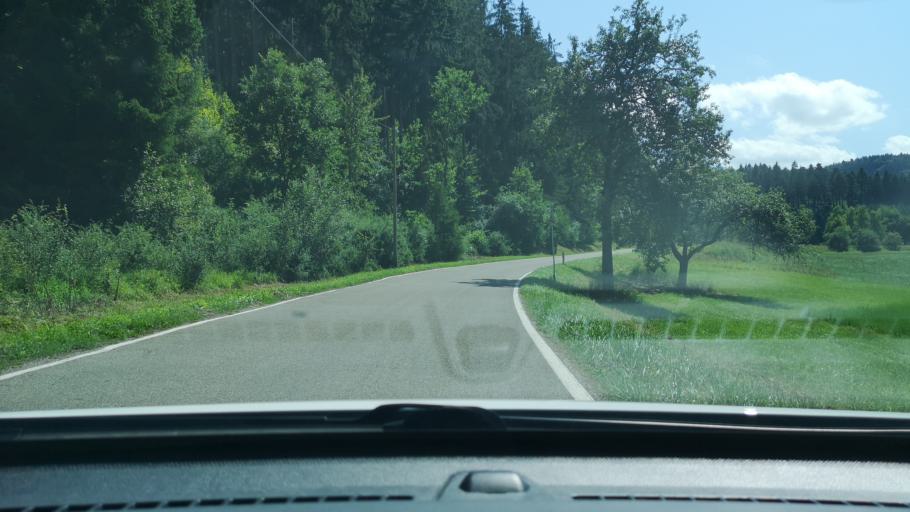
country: DE
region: Baden-Wuerttemberg
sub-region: Freiburg Region
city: Muhlheim am Bach
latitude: 48.3596
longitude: 8.7142
